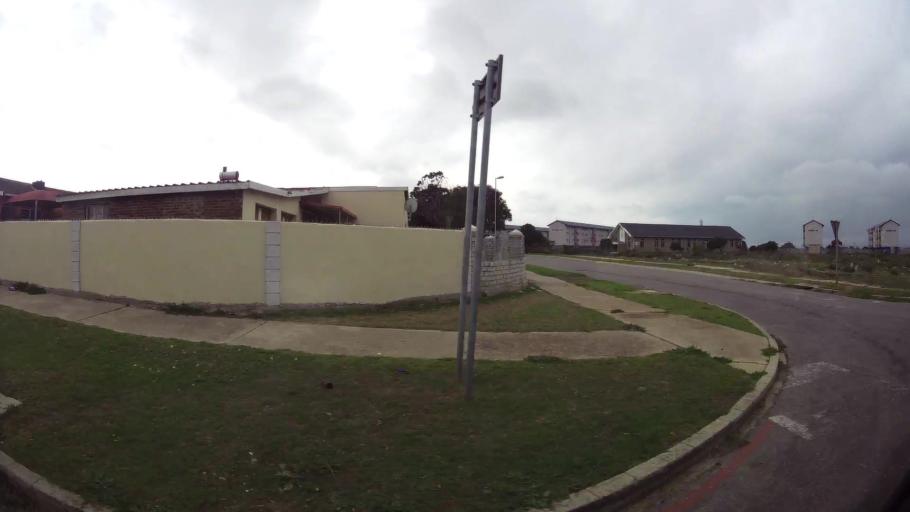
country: ZA
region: Eastern Cape
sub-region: Nelson Mandela Bay Metropolitan Municipality
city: Port Elizabeth
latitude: -33.9020
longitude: 25.5541
